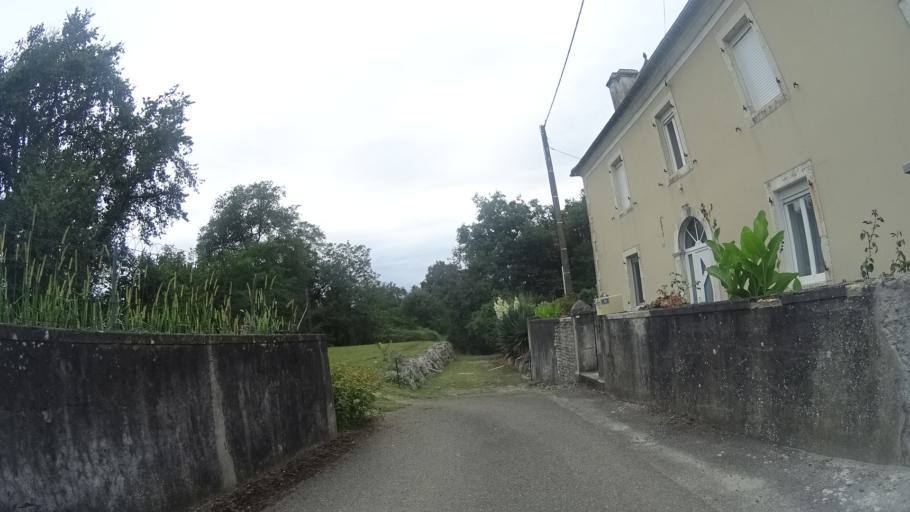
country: FR
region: Aquitaine
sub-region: Departement des Pyrenees-Atlantiques
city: Orthez
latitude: 43.4701
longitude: -0.7211
